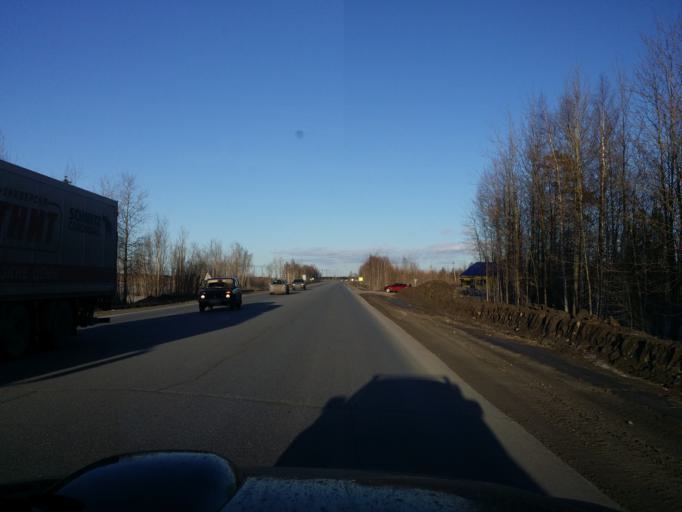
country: RU
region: Khanty-Mansiyskiy Avtonomnyy Okrug
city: Megion
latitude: 61.0686
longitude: 76.2334
